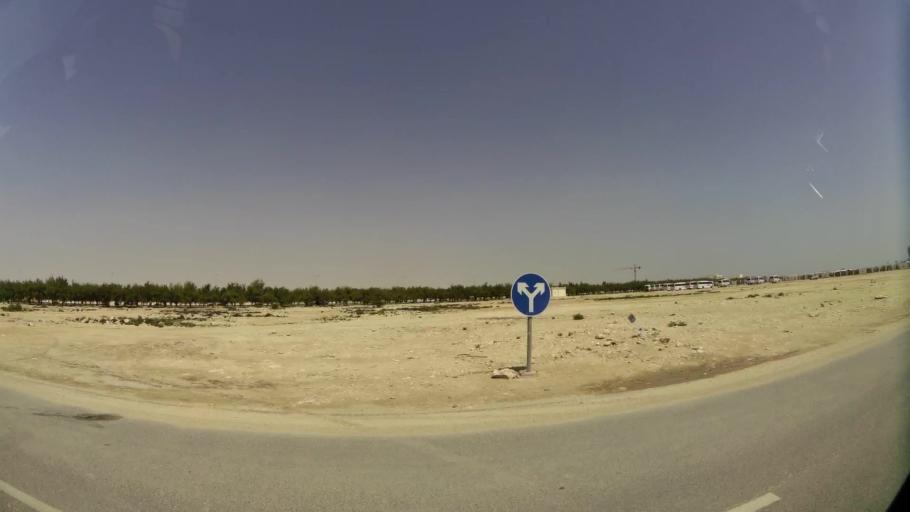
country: QA
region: Baladiyat Umm Salal
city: Umm Salal Muhammad
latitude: 25.3796
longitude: 51.4771
